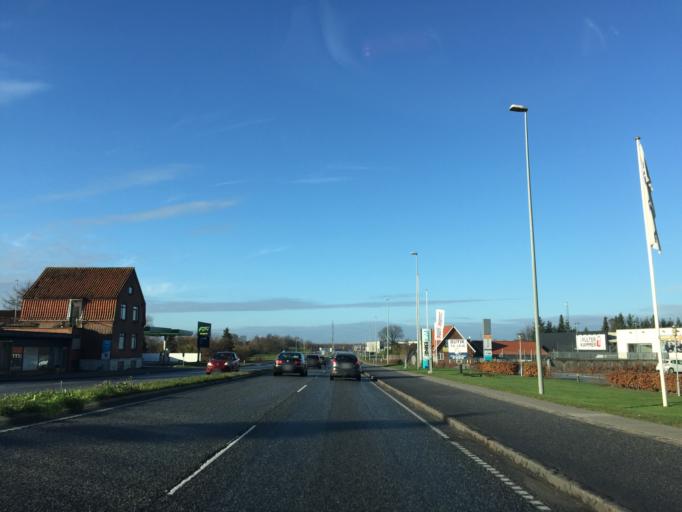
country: DK
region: Central Jutland
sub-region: Arhus Kommune
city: Stavtrup
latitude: 56.1720
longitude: 10.1553
